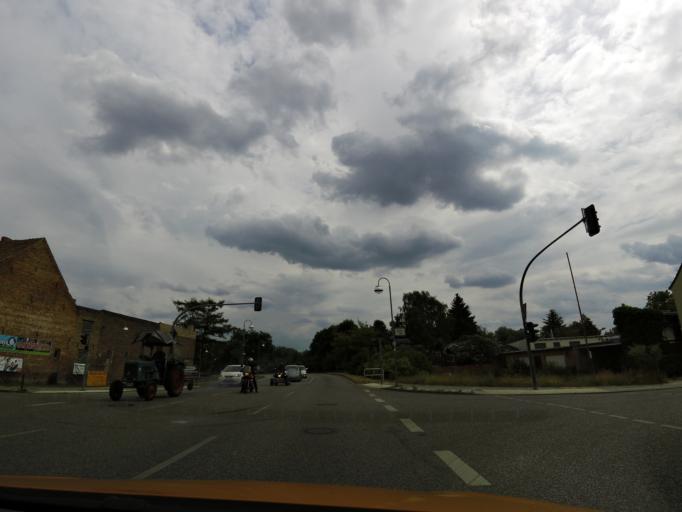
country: DE
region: Brandenburg
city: Zossen
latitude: 52.2144
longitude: 13.4462
